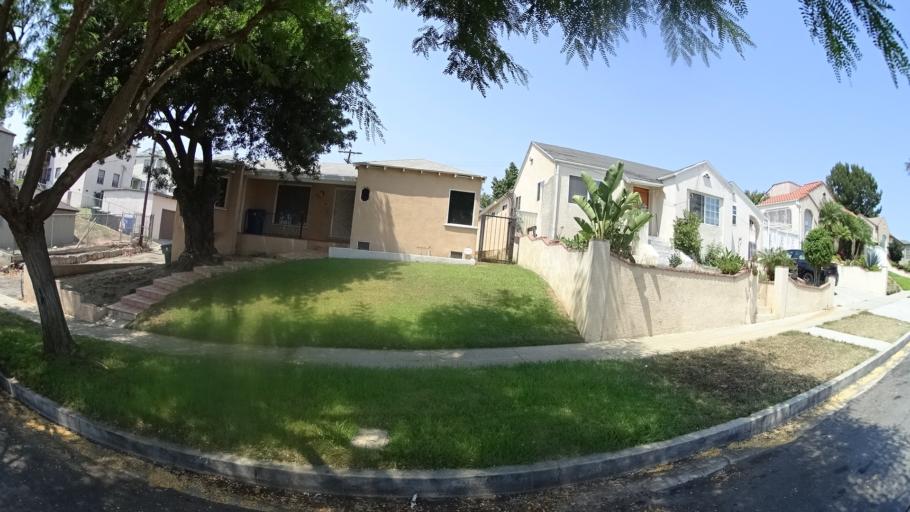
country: US
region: California
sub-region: Los Angeles County
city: View Park-Windsor Hills
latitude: 33.9817
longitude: -118.3546
